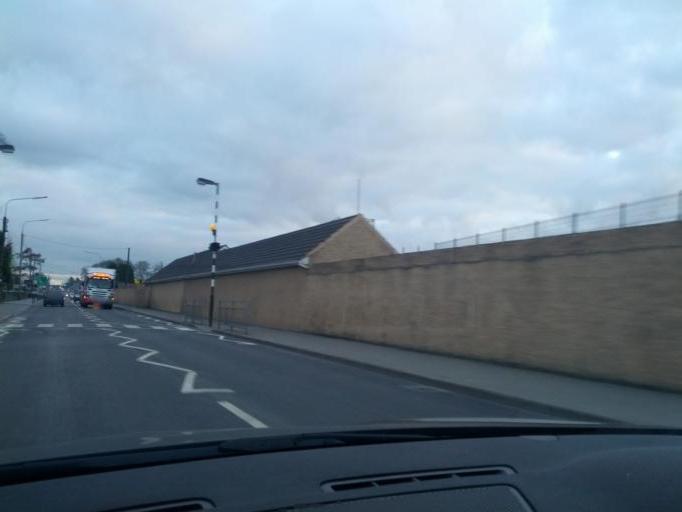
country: IE
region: Leinster
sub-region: Uibh Fhaili
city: Birr
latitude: 53.0919
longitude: -7.9077
